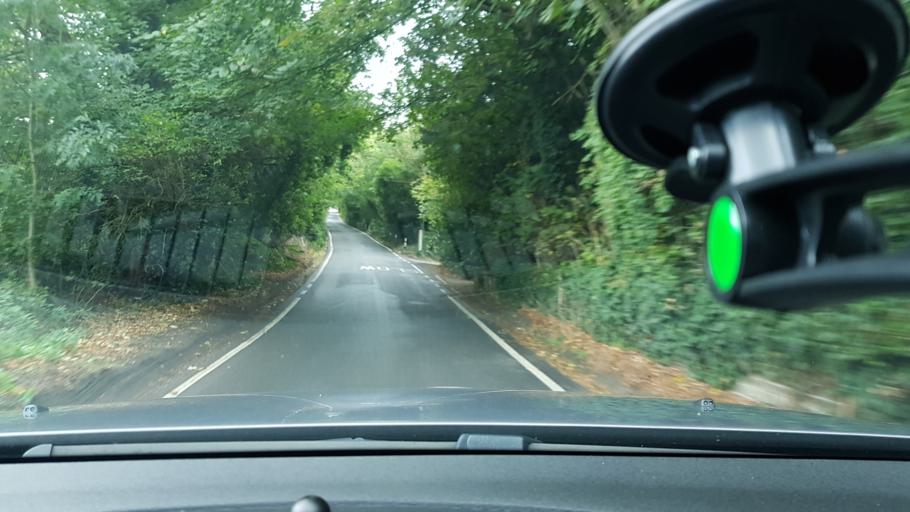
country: GB
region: England
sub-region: Hertfordshire
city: Chorleywood
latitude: 51.6533
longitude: -0.4783
